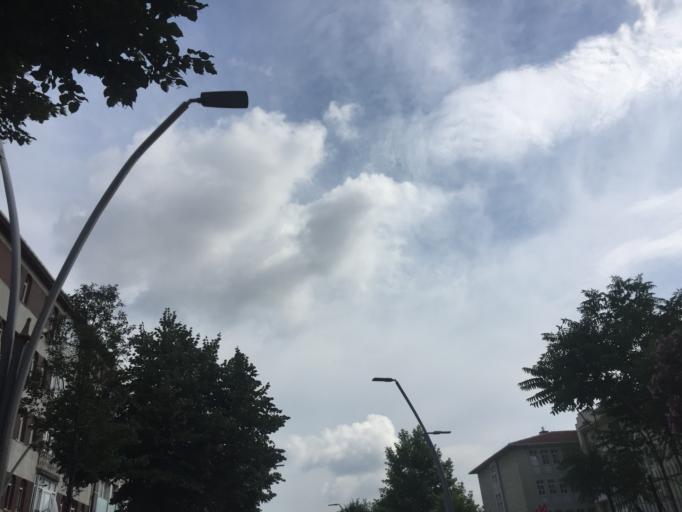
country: TR
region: Istanbul
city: Zeytinburnu
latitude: 41.0022
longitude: 28.9043
